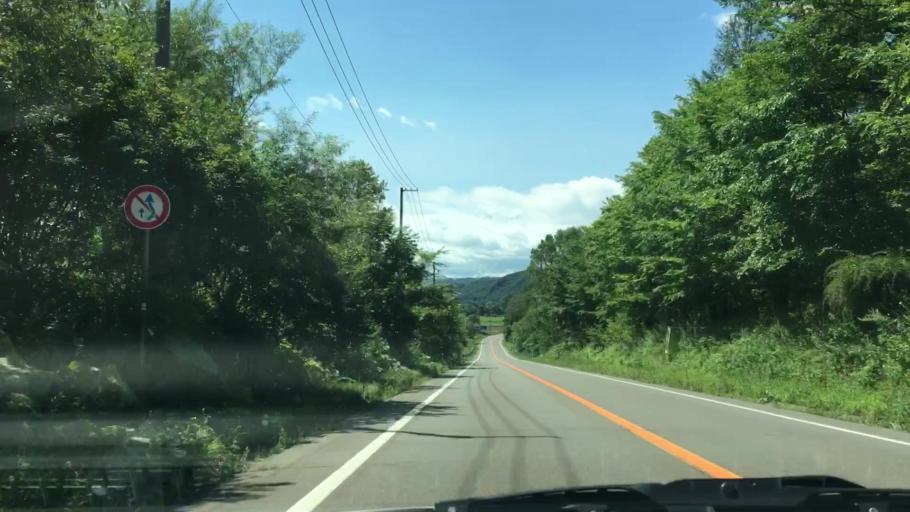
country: JP
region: Hokkaido
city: Otofuke
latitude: 43.2702
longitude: 143.5967
